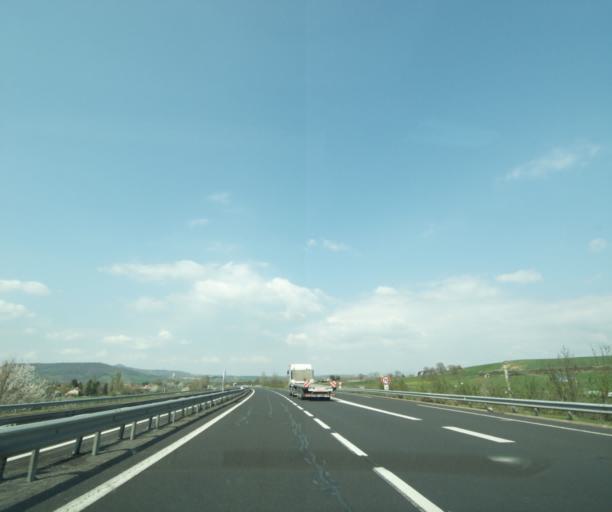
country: FR
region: Auvergne
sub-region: Departement de la Haute-Loire
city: Lempdes-sur-Allagnon
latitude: 45.3745
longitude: 3.2859
